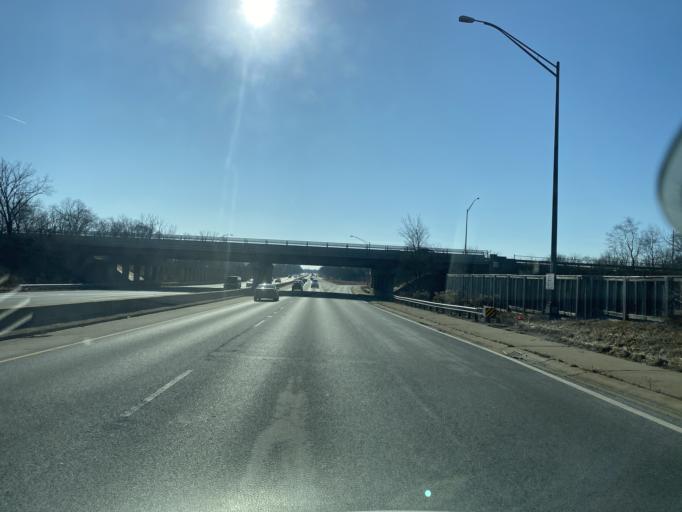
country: US
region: Illinois
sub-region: DuPage County
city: Clarendon Hills
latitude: 41.7895
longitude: -87.9471
